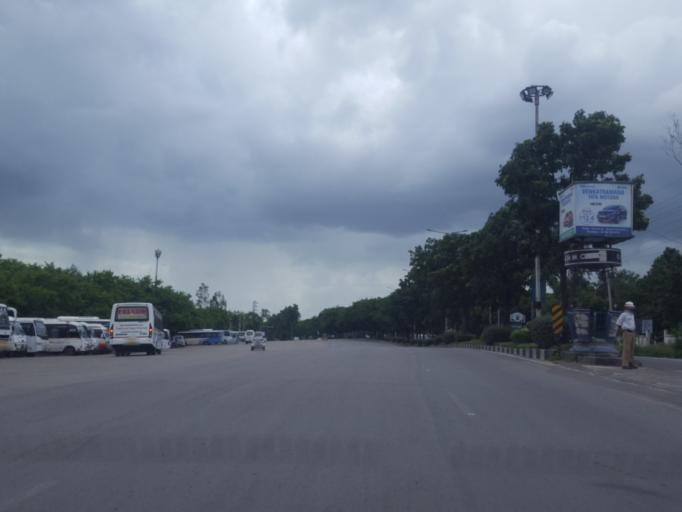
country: IN
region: Telangana
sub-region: Medak
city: Serilingampalle
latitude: 17.4493
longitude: 78.3483
